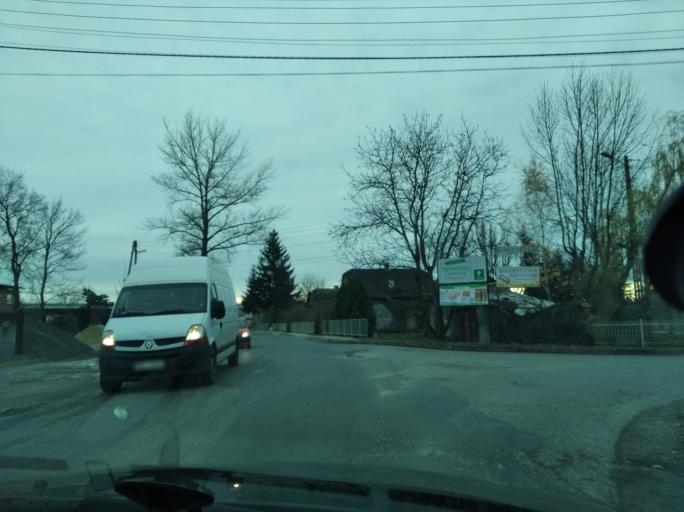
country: PL
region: Subcarpathian Voivodeship
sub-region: Powiat lancucki
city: Czarna
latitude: 50.0922
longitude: 22.1841
